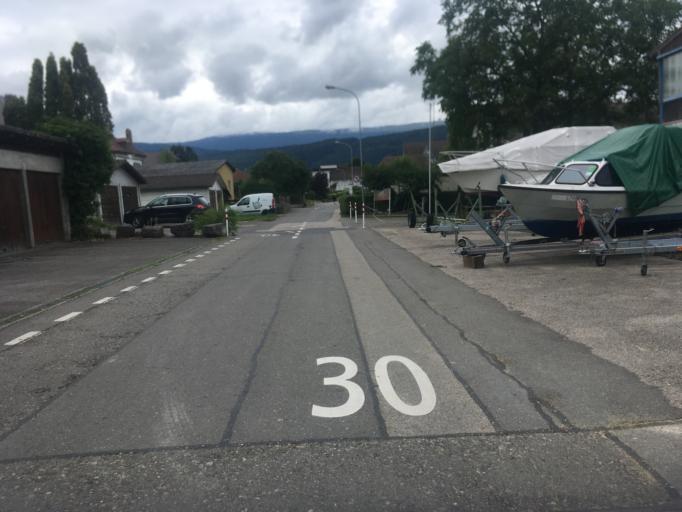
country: CH
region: Bern
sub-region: Seeland District
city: Erlach
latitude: 47.0435
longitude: 7.0999
